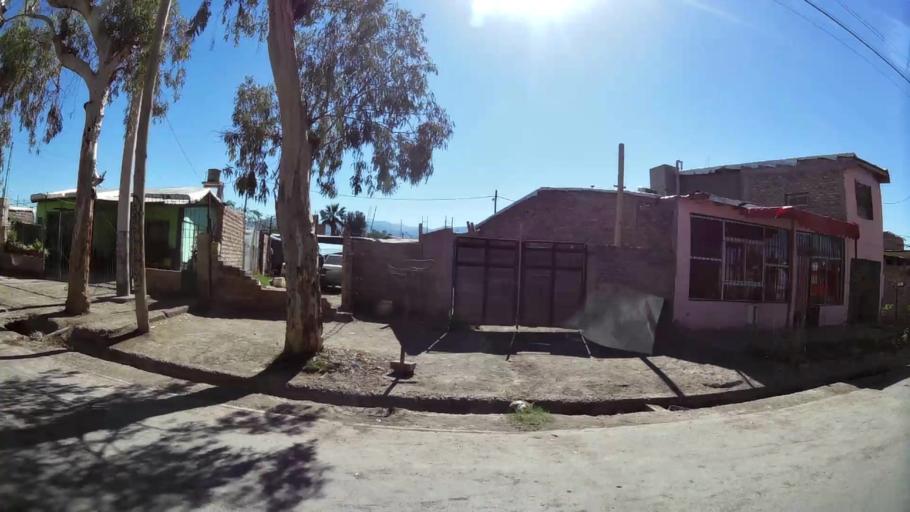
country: AR
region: Mendoza
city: Las Heras
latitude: -32.8302
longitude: -68.8165
